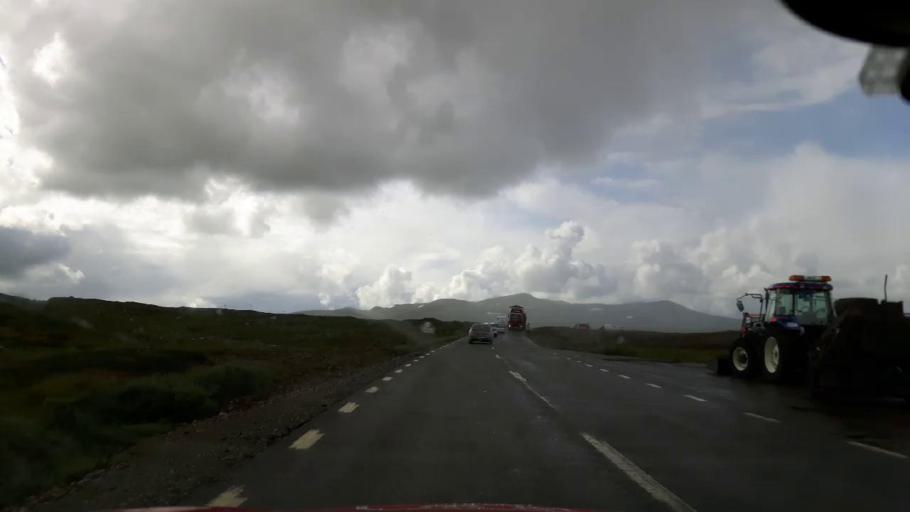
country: NO
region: Nordland
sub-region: Hattfjelldal
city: Hattfjelldal
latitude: 65.0947
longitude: 14.4654
